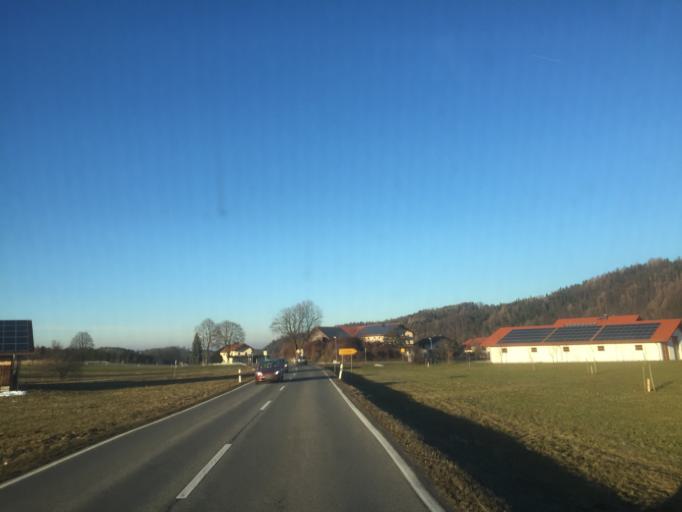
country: DE
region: Bavaria
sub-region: Upper Bavaria
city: Siegsdorf
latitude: 47.8366
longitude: 12.6353
